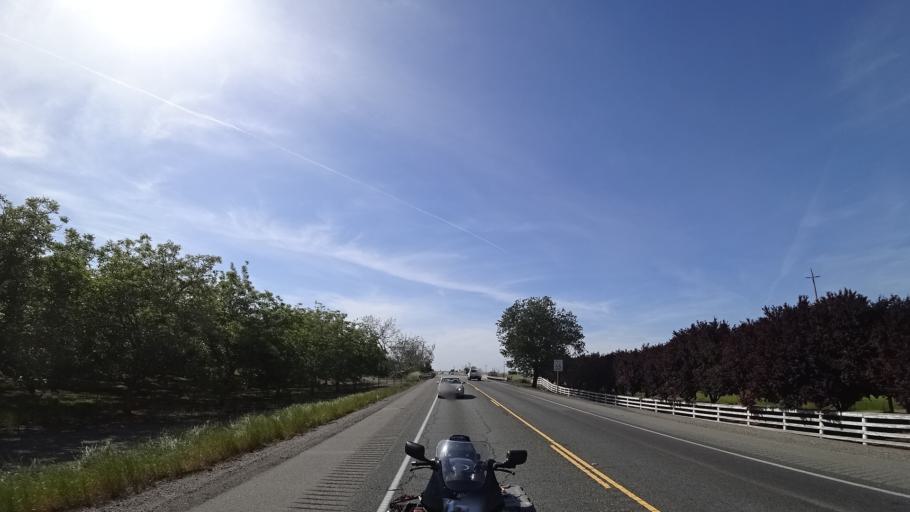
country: US
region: California
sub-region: Glenn County
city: Hamilton City
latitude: 39.8855
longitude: -121.9788
